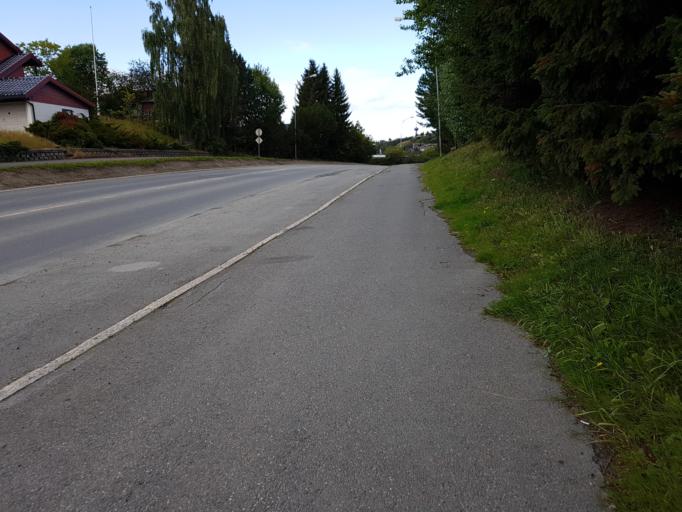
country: NO
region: Sor-Trondelag
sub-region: Trondheim
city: Trondheim
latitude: 63.4005
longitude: 10.4228
